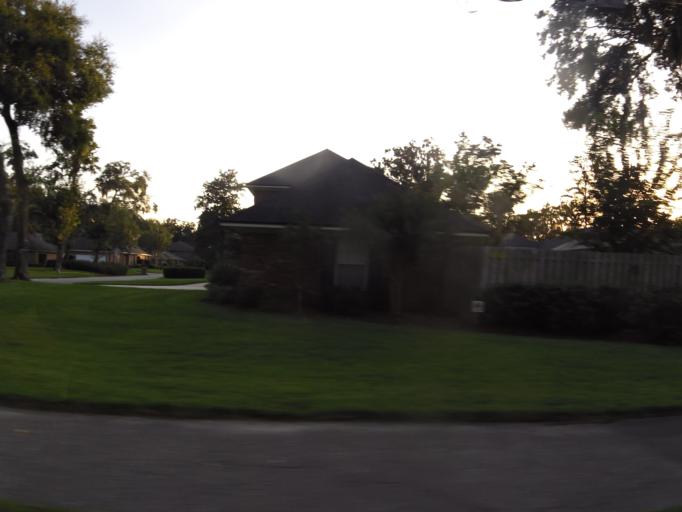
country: US
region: Florida
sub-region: Clay County
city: Orange Park
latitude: 30.1987
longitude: -81.6336
